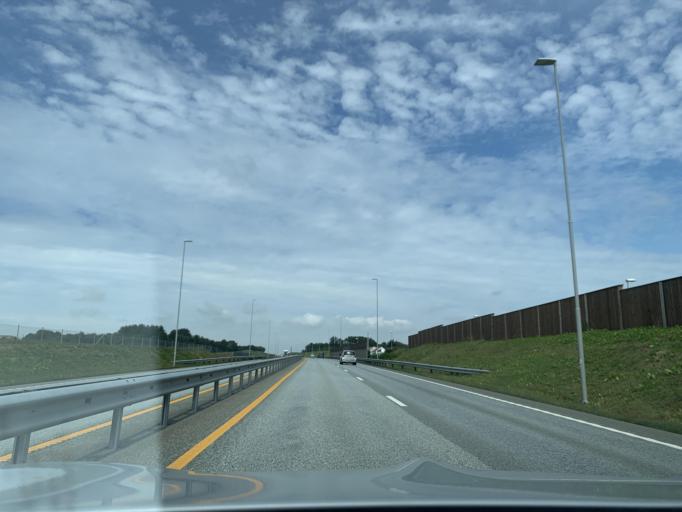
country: NO
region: Rogaland
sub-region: Sandnes
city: Sandnes
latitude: 58.8295
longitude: 5.7051
